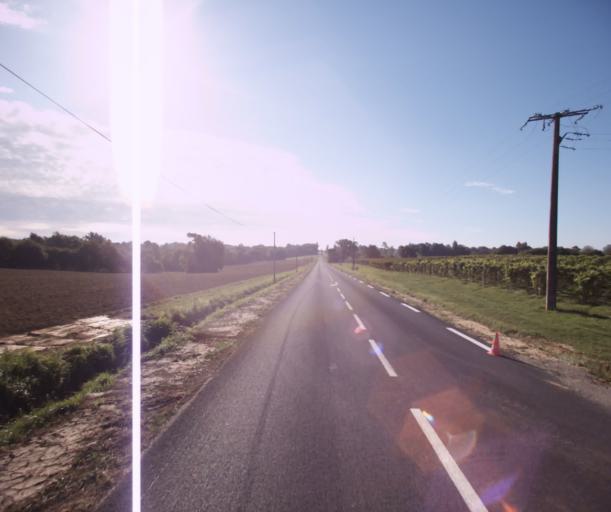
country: FR
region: Midi-Pyrenees
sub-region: Departement du Gers
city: Cazaubon
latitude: 43.8994
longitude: -0.0138
